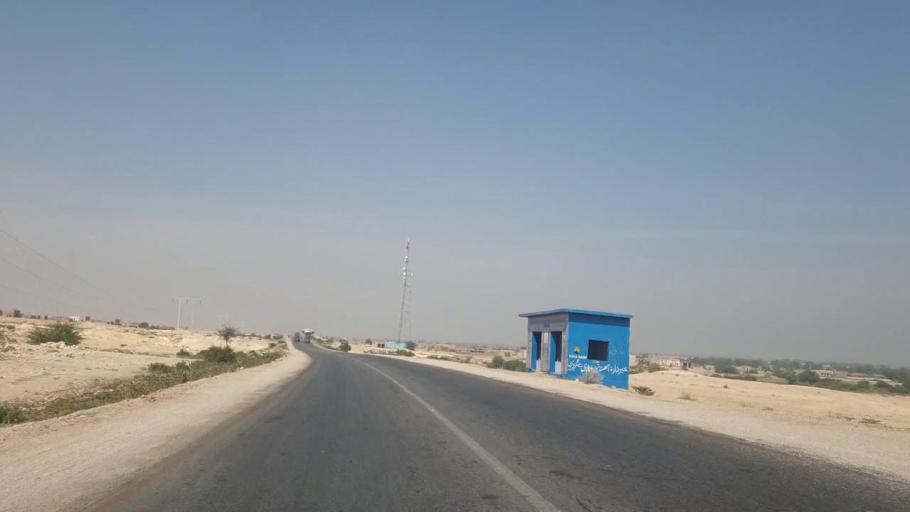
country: PK
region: Sindh
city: Hala
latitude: 25.7707
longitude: 68.2861
